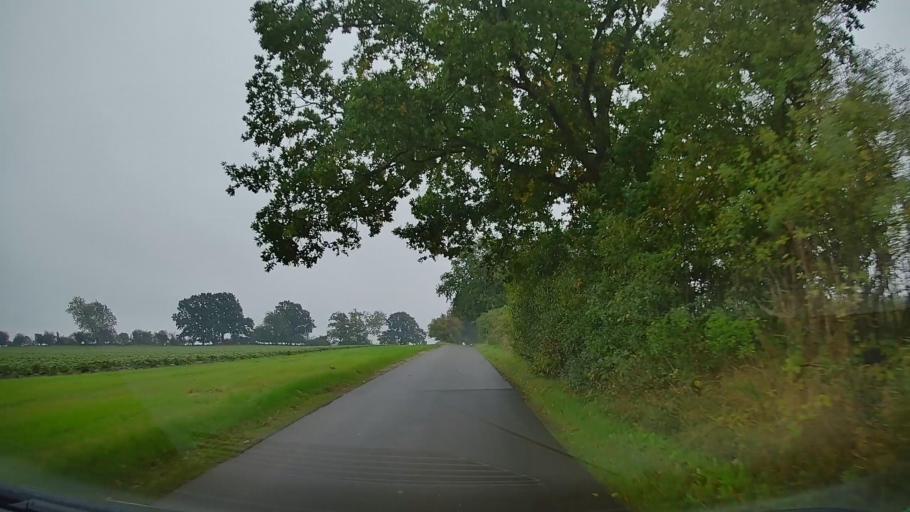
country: DE
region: Mecklenburg-Vorpommern
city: Gramkow
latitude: 53.9249
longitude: 11.3417
